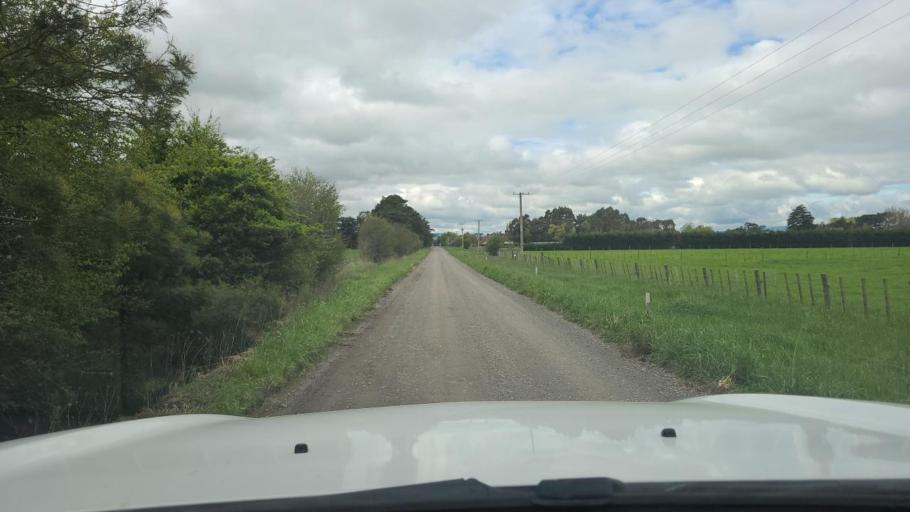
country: NZ
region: Wellington
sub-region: South Wairarapa District
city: Waipawa
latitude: -41.1438
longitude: 175.3750
